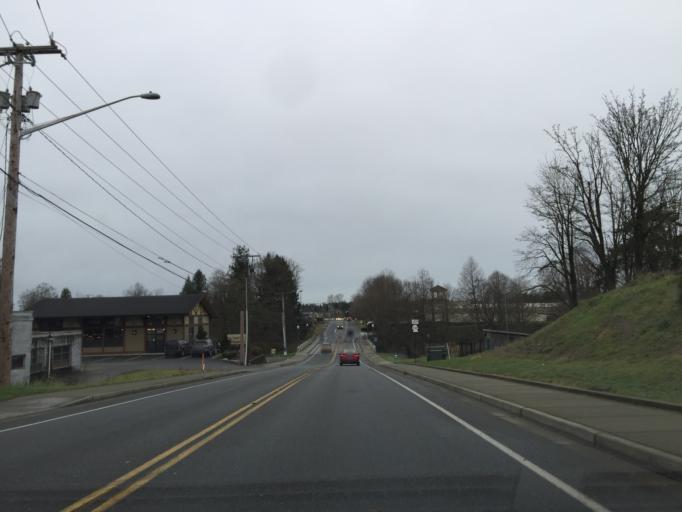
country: US
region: Washington
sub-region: Whatcom County
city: Lynden
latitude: 48.9355
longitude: -122.4790
